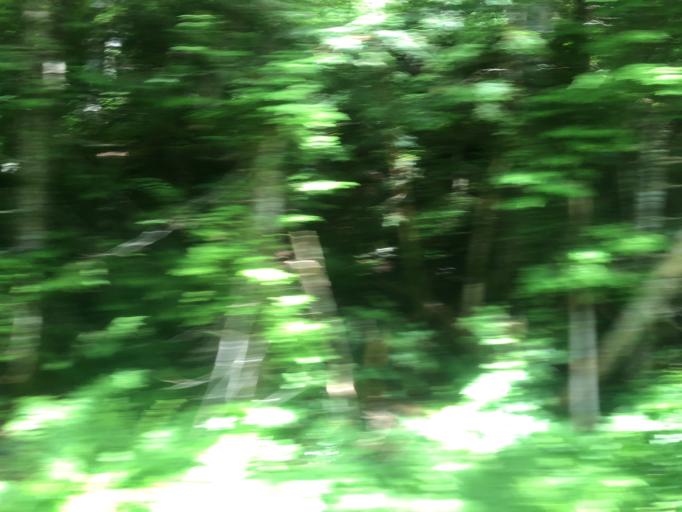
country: US
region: Oregon
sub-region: Clackamas County
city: Mount Hood Village
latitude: 45.4702
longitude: -121.8573
